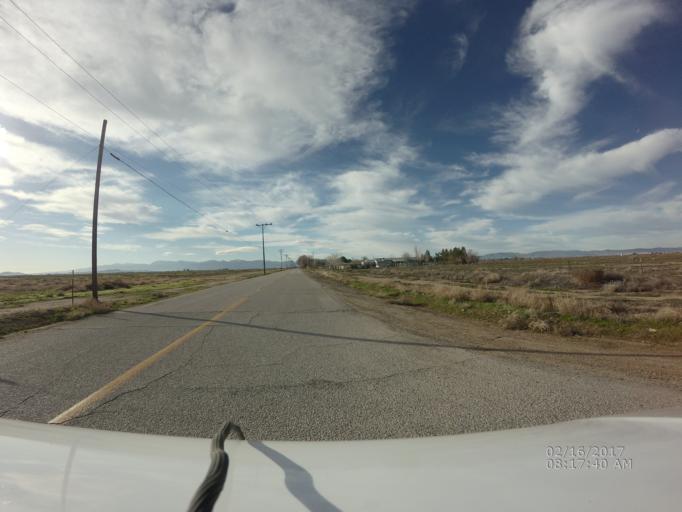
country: US
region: California
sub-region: Los Angeles County
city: Lancaster
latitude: 34.7633
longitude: -118.0055
